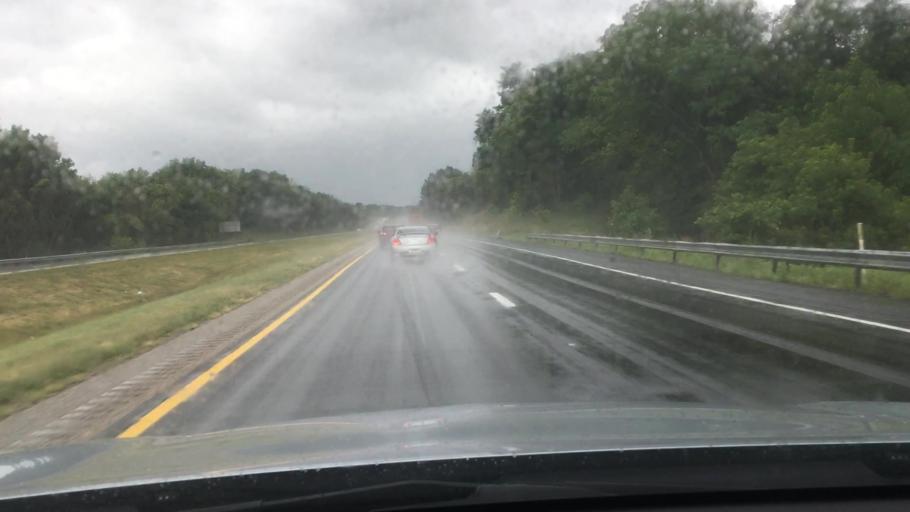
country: US
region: Pennsylvania
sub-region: Cumberland County
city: Shippensburg
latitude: 40.0706
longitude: -77.4615
